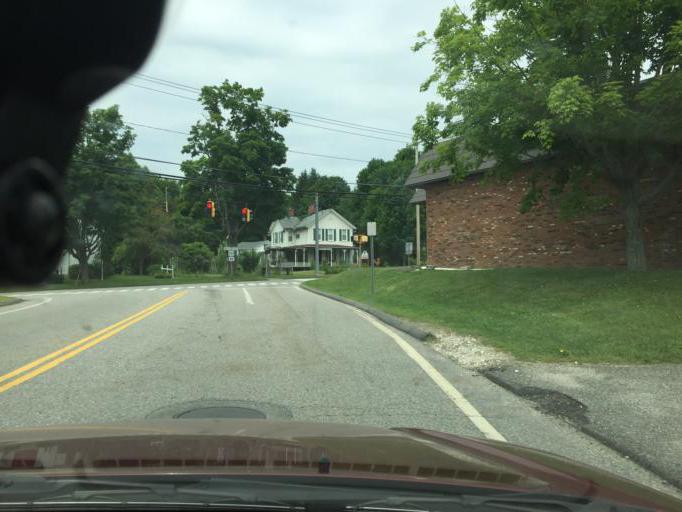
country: US
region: Connecticut
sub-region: Litchfield County
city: Litchfield
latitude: 41.7240
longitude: -73.2364
